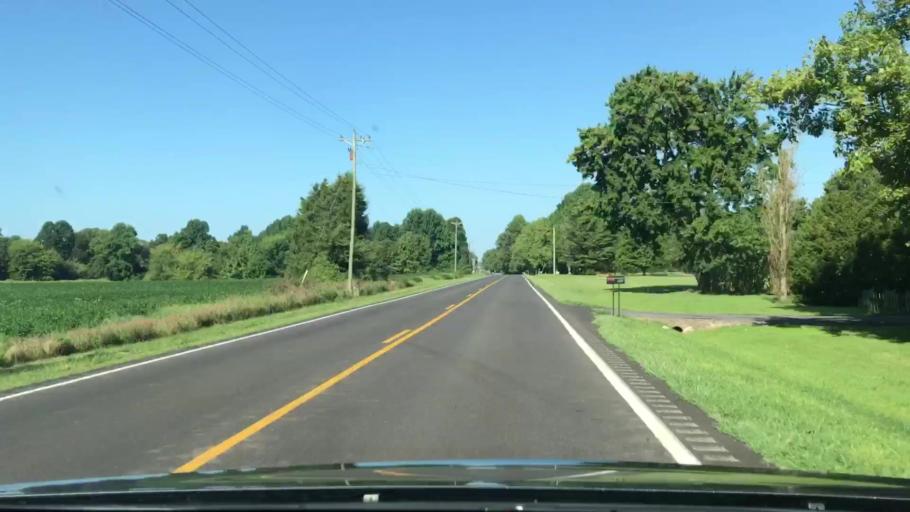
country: US
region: Kentucky
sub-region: Marshall County
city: Benton
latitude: 36.7650
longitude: -88.3868
